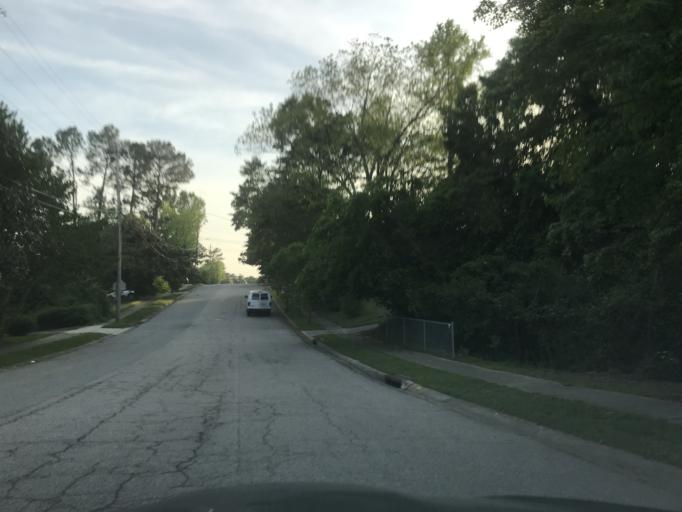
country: US
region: North Carolina
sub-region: Wake County
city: Raleigh
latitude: 35.7957
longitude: -78.6054
